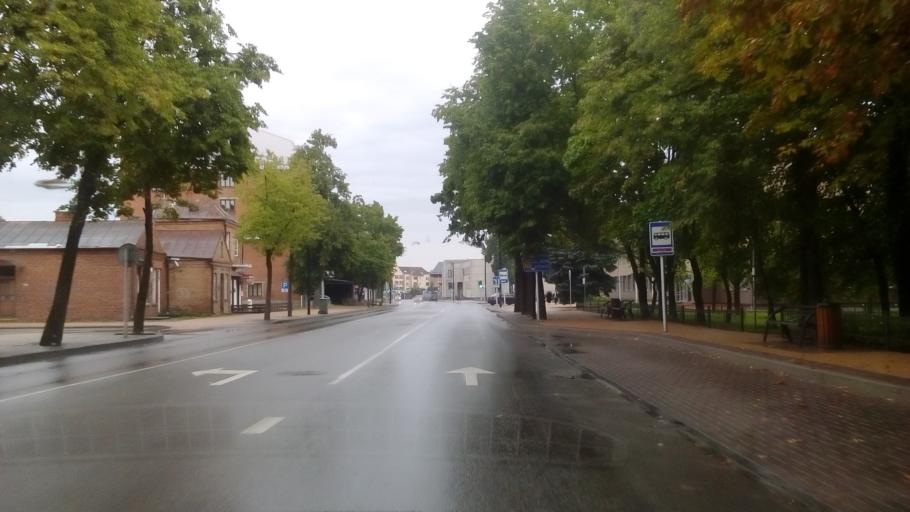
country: LT
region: Alytaus apskritis
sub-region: Alytus
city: Alytus
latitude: 54.3945
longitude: 24.0456
